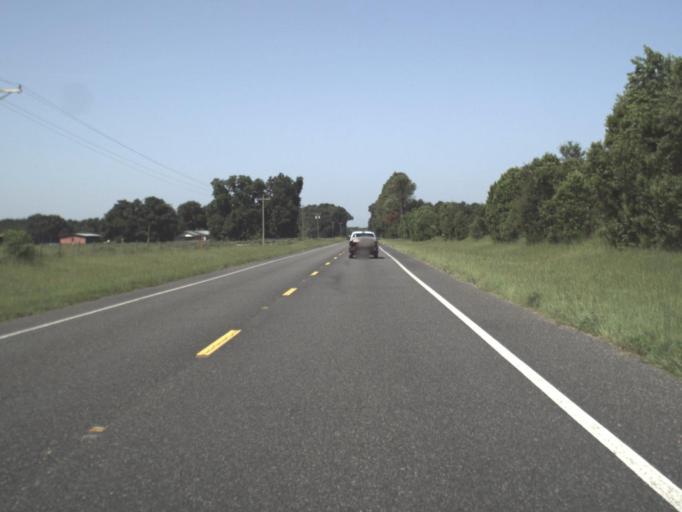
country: US
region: Florida
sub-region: Levy County
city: Chiefland
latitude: 29.4982
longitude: -82.8415
